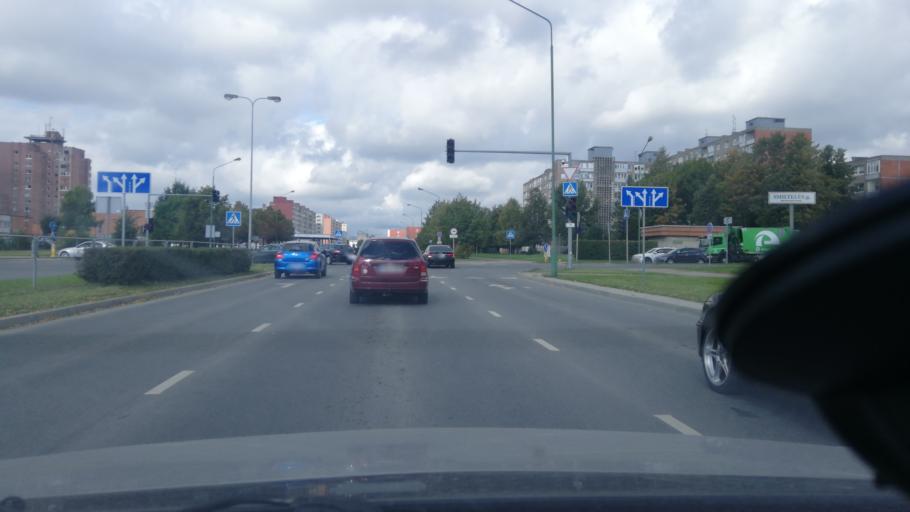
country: LT
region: Klaipedos apskritis
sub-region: Klaipeda
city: Klaipeda
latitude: 55.6702
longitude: 21.1936
